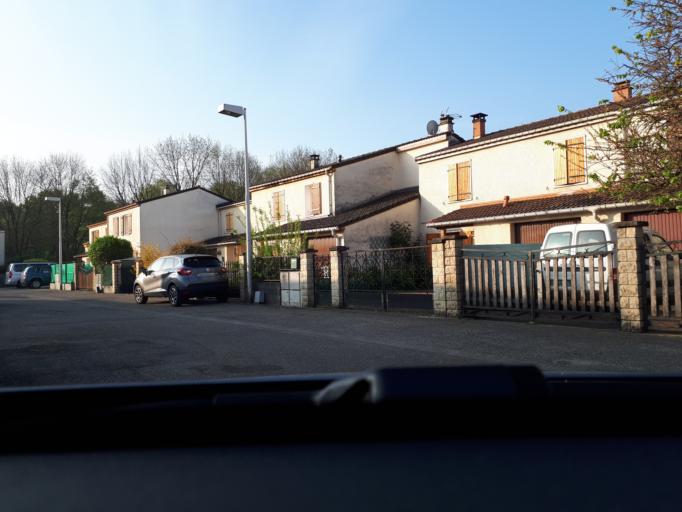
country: FR
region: Rhone-Alpes
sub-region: Departement de l'Isere
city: Bourgoin-Jallieu
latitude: 45.6113
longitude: 5.2676
